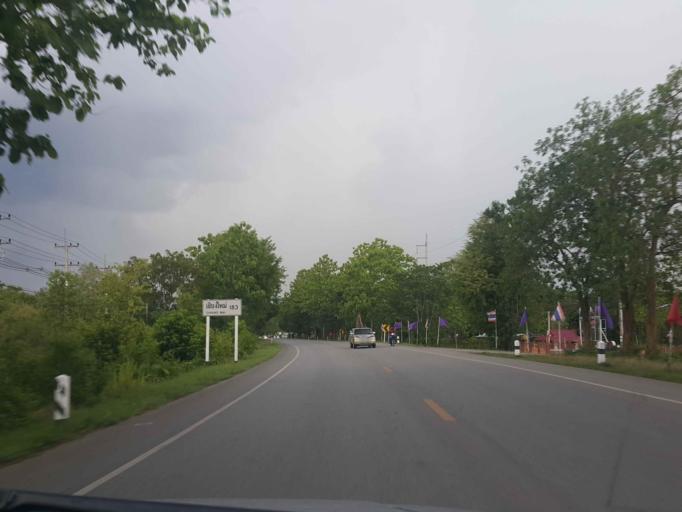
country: TH
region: Phrae
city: Den Chai
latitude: 17.9779
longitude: 100.0303
